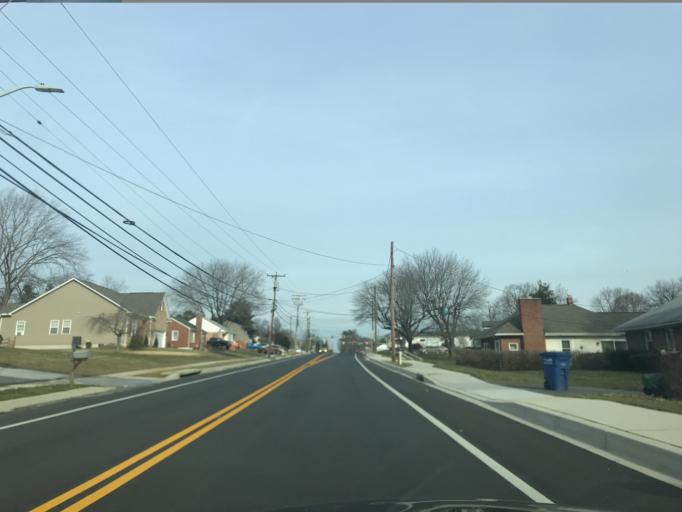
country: US
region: Maryland
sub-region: Harford County
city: Aberdeen
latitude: 39.5199
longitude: -76.1712
